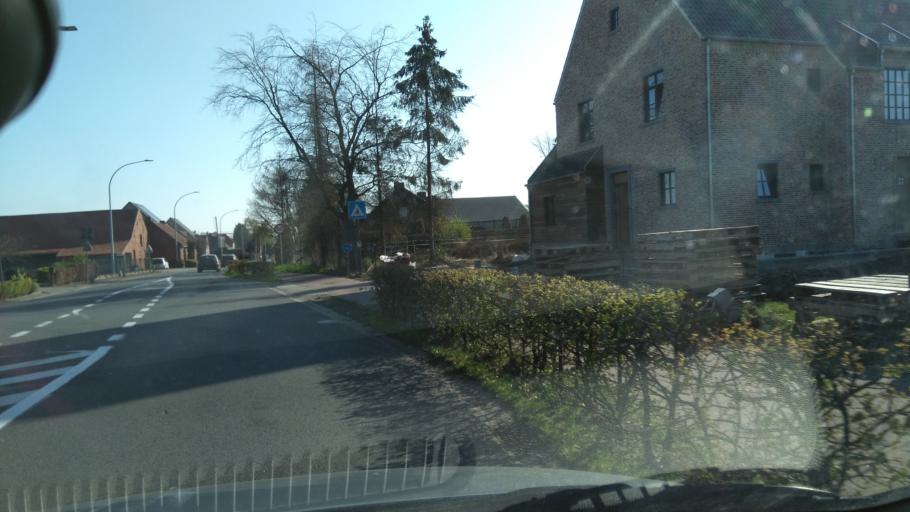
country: BE
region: Flanders
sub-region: Provincie Antwerpen
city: Ravels
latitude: 51.4054
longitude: 4.9857
